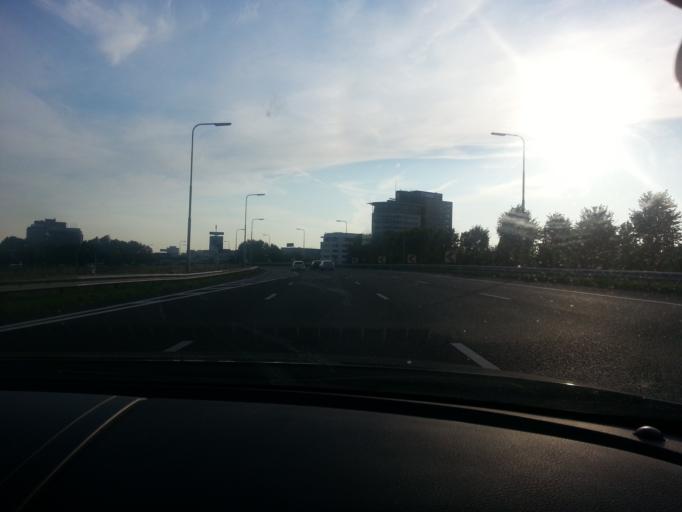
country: NL
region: South Holland
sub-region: Gemeente Den Haag
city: Ypenburg
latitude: 52.0471
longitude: 4.3521
